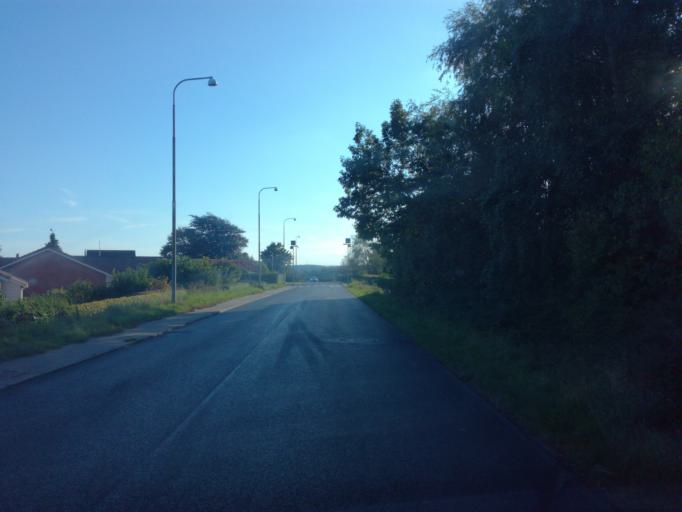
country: DK
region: South Denmark
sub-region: Fredericia Kommune
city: Taulov
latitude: 55.5353
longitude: 9.6049
